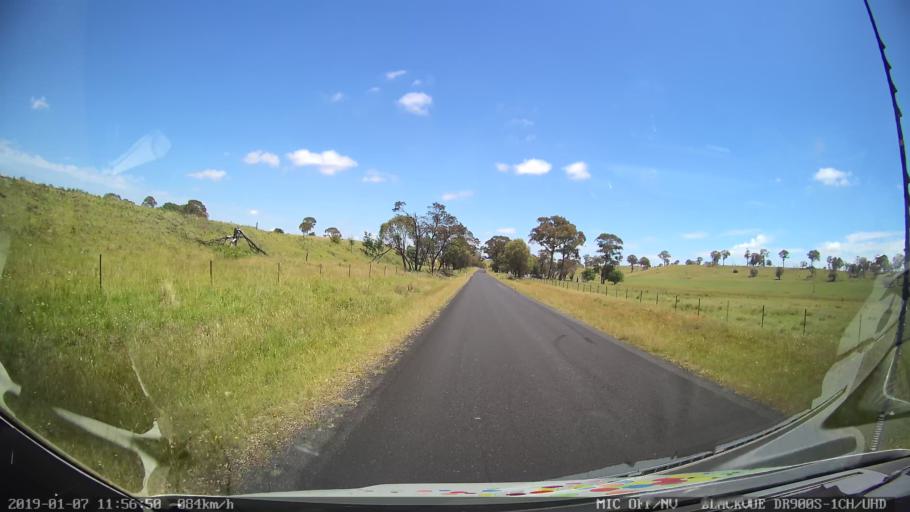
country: AU
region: New South Wales
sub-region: Guyra
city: Guyra
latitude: -30.2706
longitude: 151.6704
